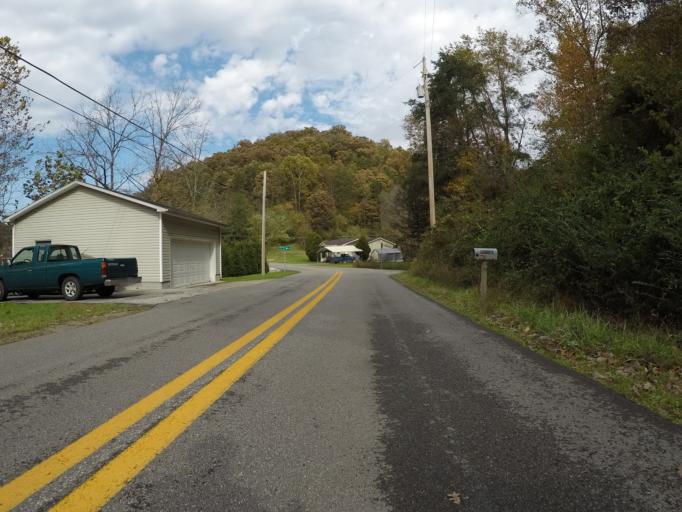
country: US
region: West Virginia
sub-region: Wayne County
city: Lavalette
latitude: 38.3444
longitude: -82.4496
